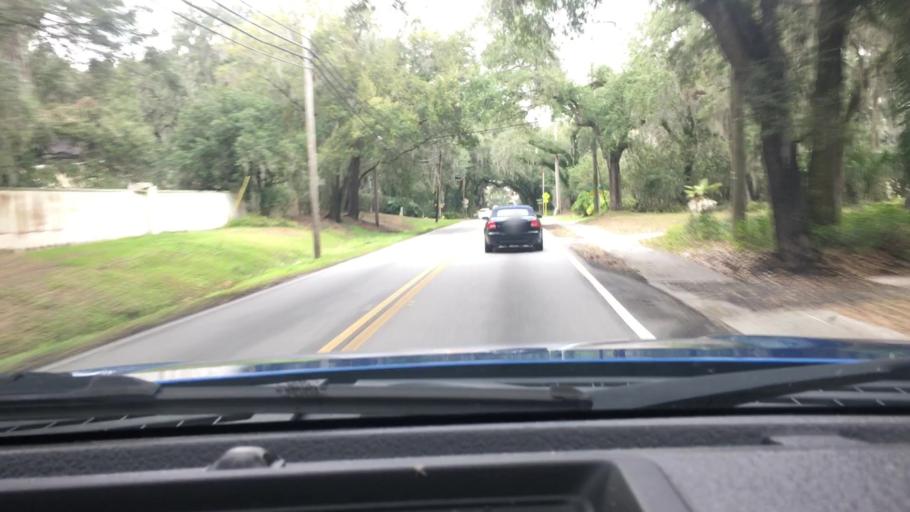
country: US
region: Florida
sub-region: Hillsborough County
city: Mango
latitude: 27.9562
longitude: -82.3104
